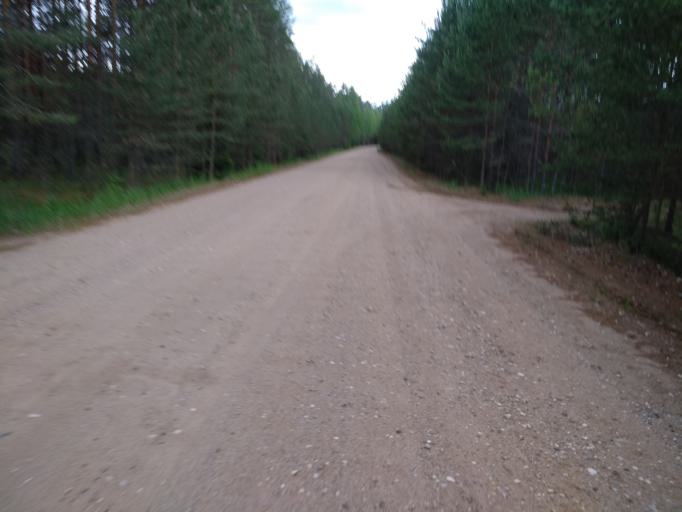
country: RU
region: Tverskaya
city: Krasnomayskiy
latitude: 57.5349
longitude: 34.2971
